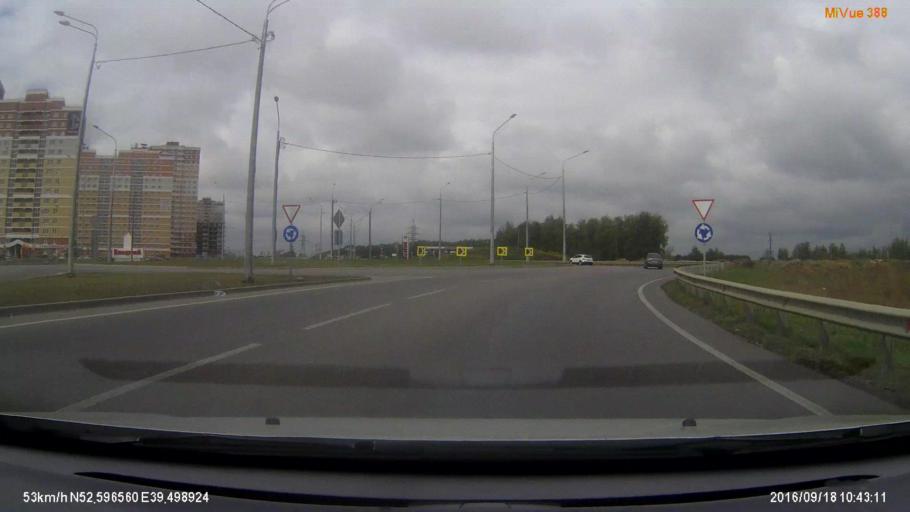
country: RU
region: Lipetsk
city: Syrskoye
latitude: 52.5964
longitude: 39.4993
